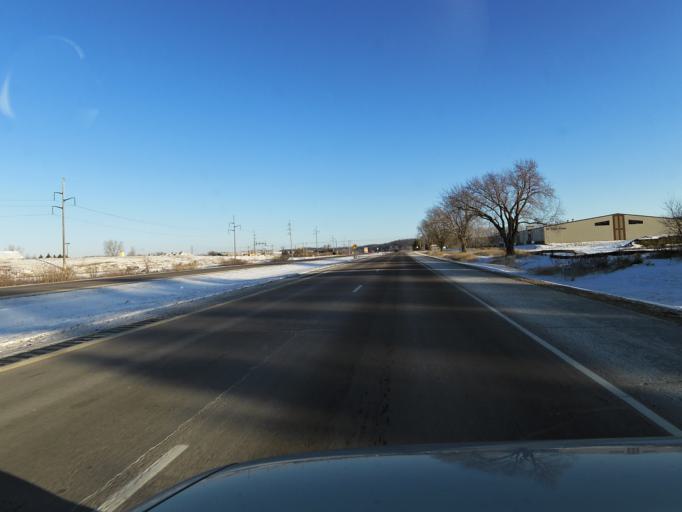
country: US
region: Minnesota
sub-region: Scott County
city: Jordan
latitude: 44.7113
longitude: -93.5903
